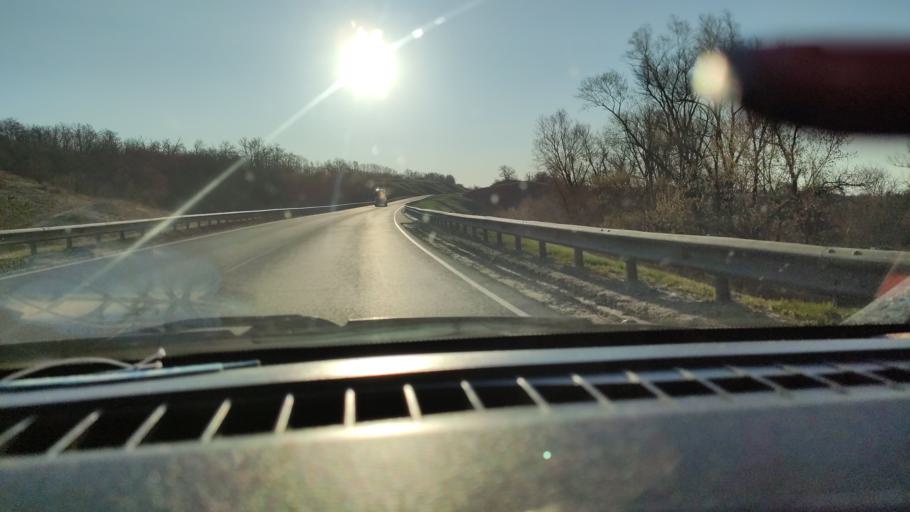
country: RU
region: Saratov
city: Tersa
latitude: 52.1037
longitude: 47.4887
